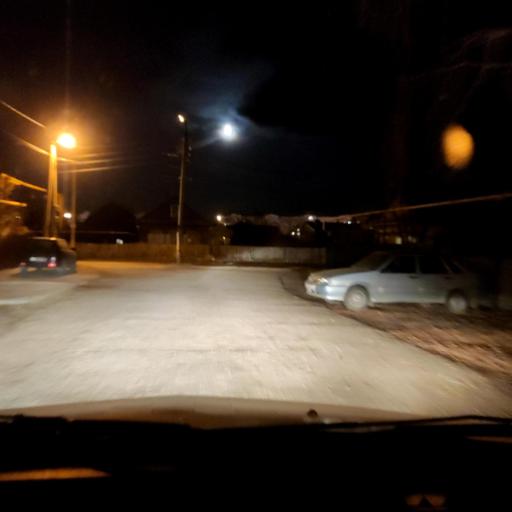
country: RU
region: Bashkortostan
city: Ufa
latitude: 54.7781
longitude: 56.0636
